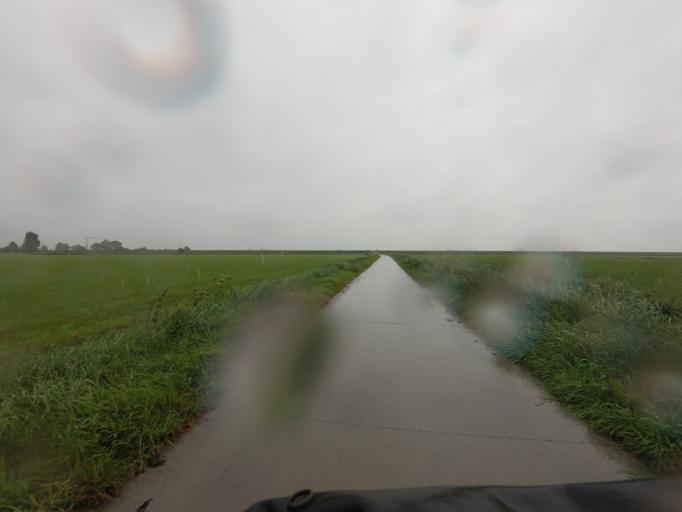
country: NL
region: Friesland
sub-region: Sudwest Fryslan
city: Bolsward
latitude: 53.0018
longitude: 5.5289
